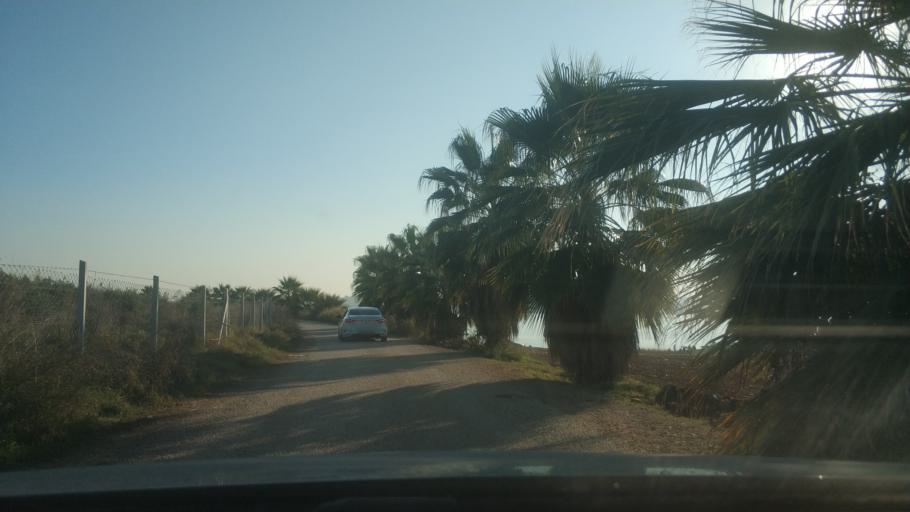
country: TR
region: Adana
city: Adana
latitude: 37.0914
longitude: 35.3012
